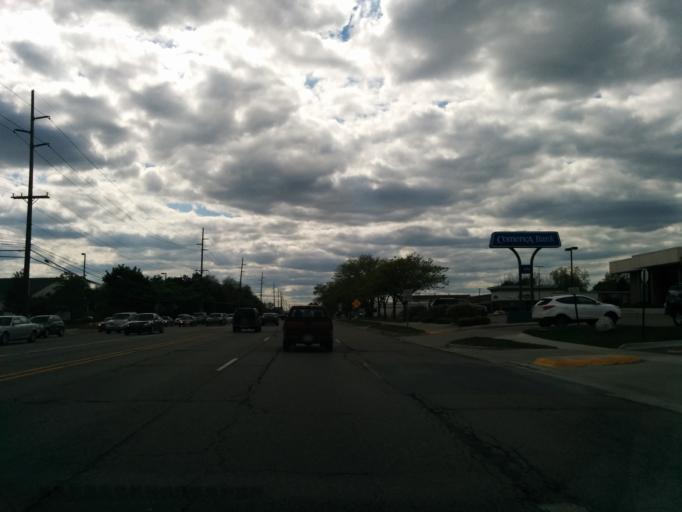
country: US
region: Michigan
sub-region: Oakland County
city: Farmington Hills
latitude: 42.4992
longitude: -83.3591
